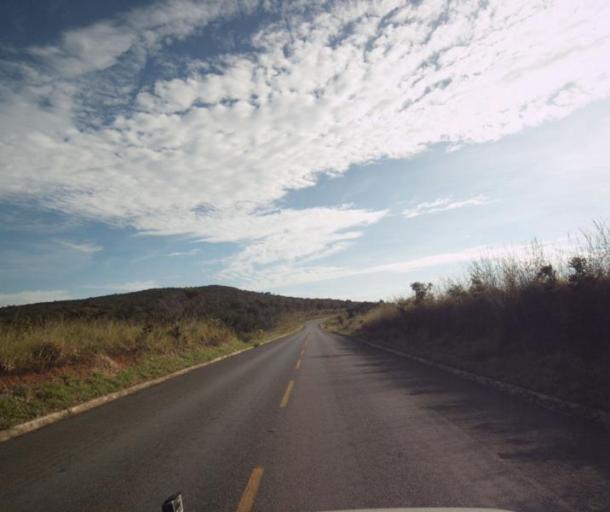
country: BR
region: Goias
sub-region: Pirenopolis
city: Pirenopolis
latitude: -15.6545
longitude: -48.6836
